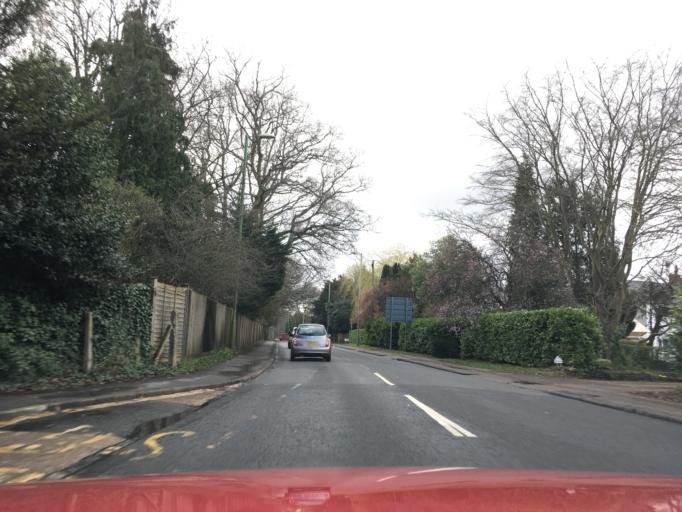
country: GB
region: England
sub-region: Hampshire
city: Chandlers Ford
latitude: 50.9743
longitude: -1.3884
